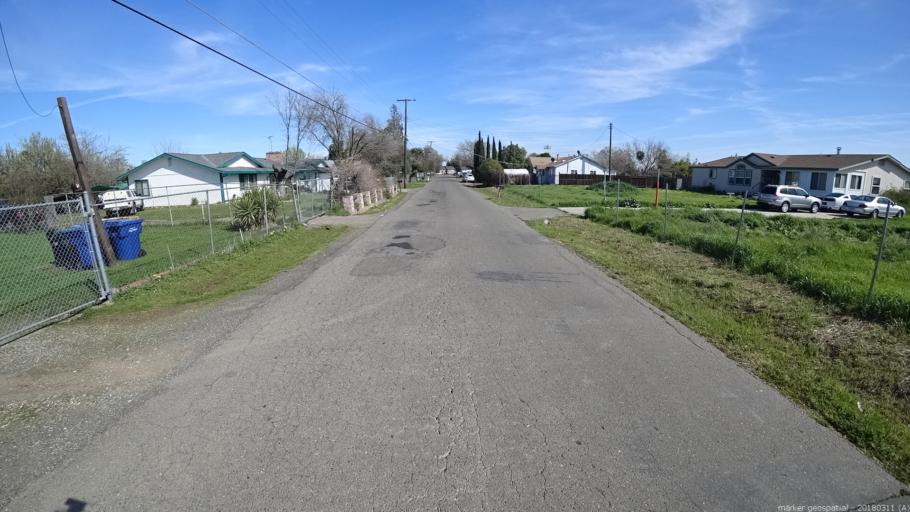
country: US
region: California
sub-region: Sacramento County
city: Florin
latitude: 38.4827
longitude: -121.4266
